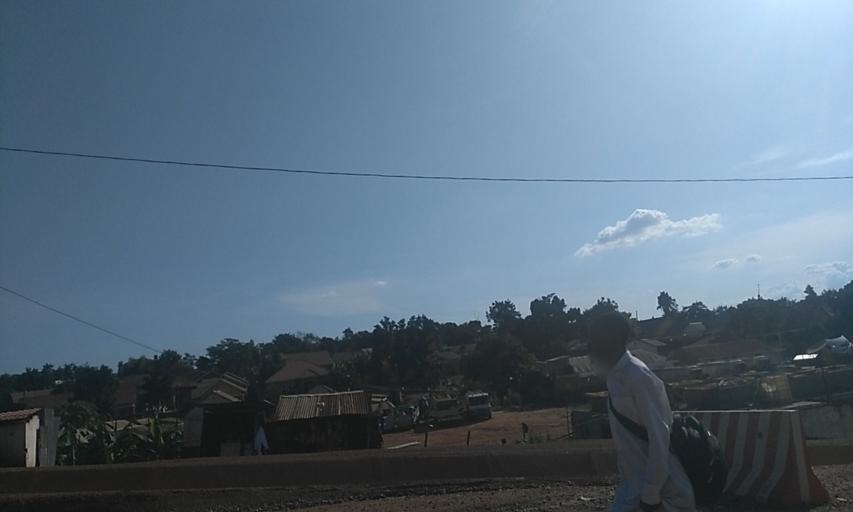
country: UG
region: Central Region
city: Kampala Central Division
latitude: 0.3313
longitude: 32.5288
